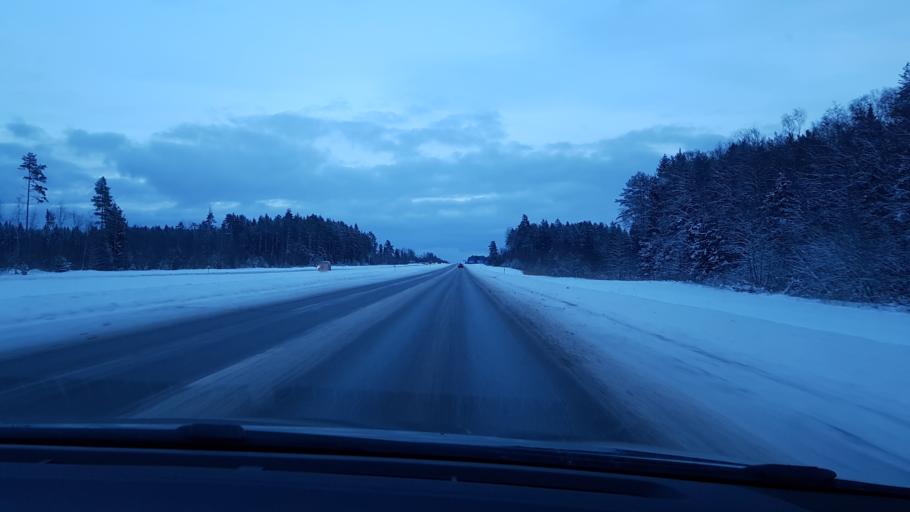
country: EE
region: Harju
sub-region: Raasiku vald
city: Raasiku
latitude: 59.4383
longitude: 25.2542
